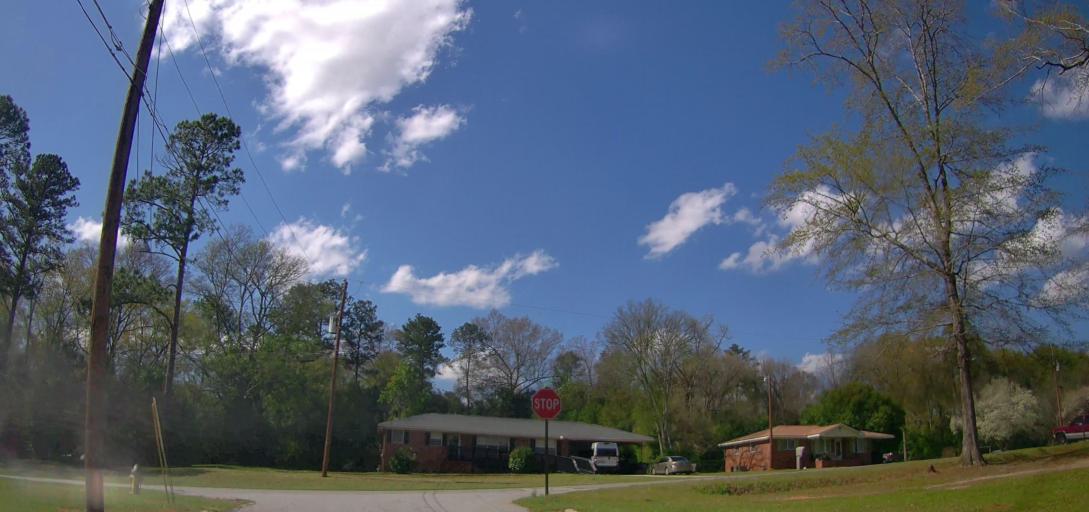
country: US
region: Georgia
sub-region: Bibb County
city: Macon
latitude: 32.8063
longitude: -83.5363
